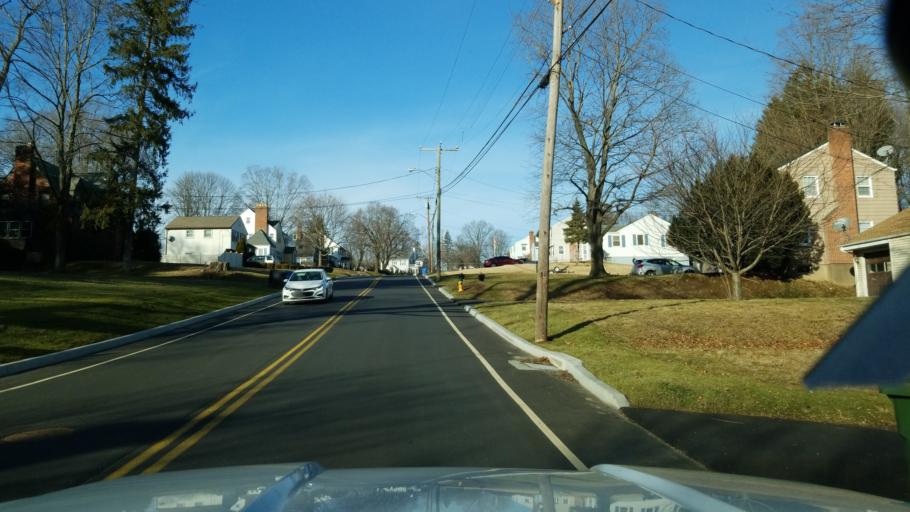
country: US
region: Connecticut
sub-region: Middlesex County
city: Middletown
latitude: 41.5560
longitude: -72.6756
